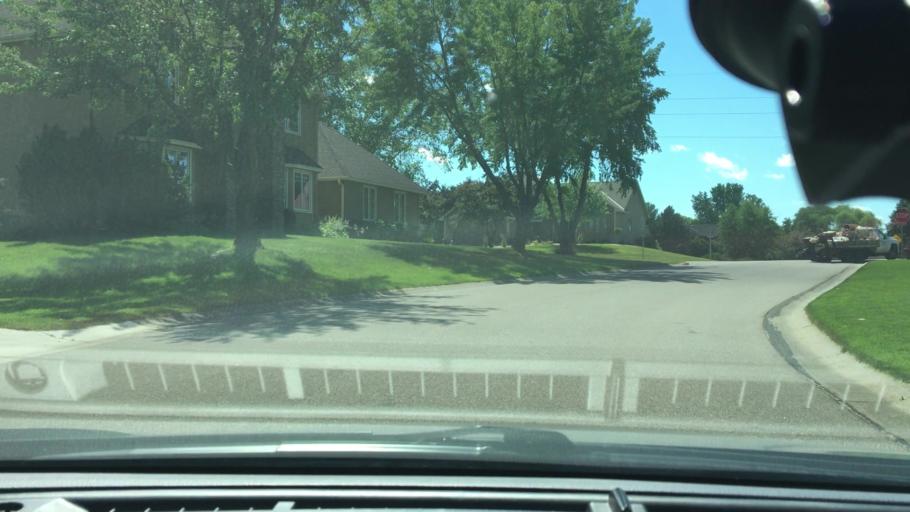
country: US
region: Minnesota
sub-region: Hennepin County
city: Maple Grove
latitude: 45.0668
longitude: -93.4601
